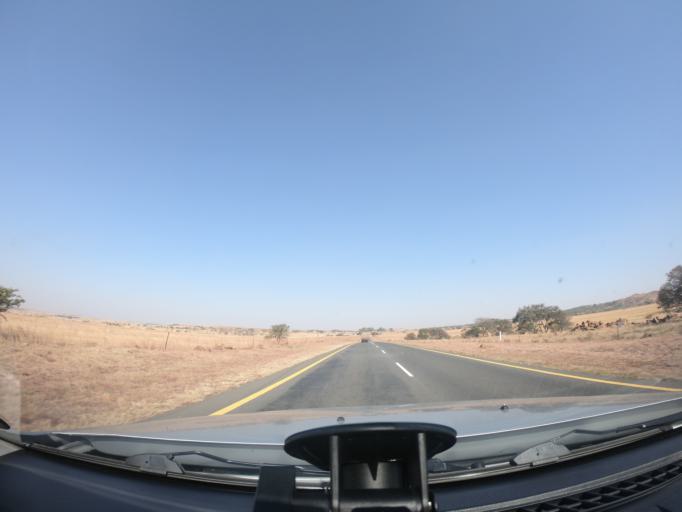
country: ZA
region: KwaZulu-Natal
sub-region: uThukela District Municipality
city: Ekuvukeni
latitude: -28.3895
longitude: 29.9371
